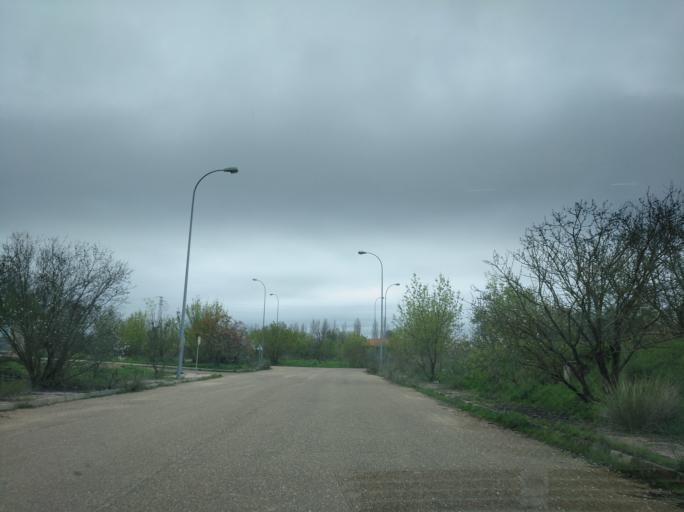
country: ES
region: Extremadura
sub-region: Provincia de Badajoz
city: Badajoz
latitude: 38.9000
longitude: -6.9663
